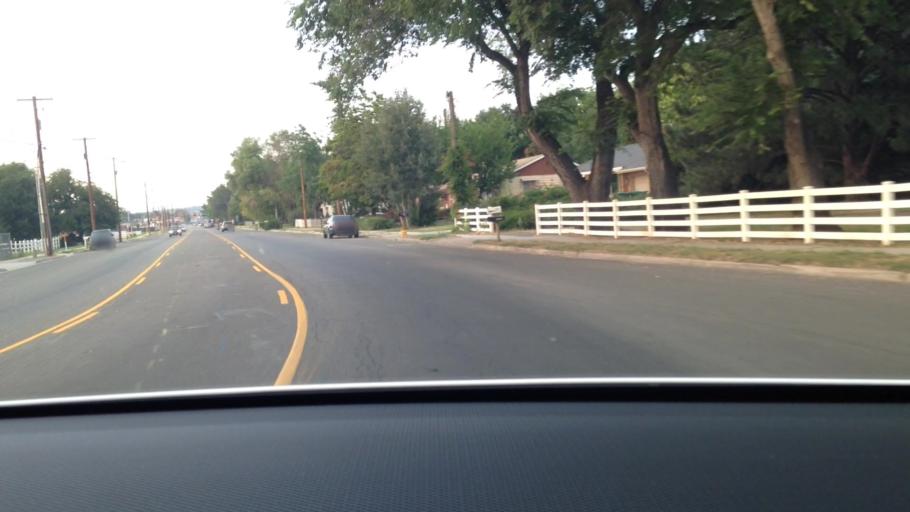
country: US
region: Utah
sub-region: Davis County
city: Layton
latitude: 41.0517
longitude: -111.9578
